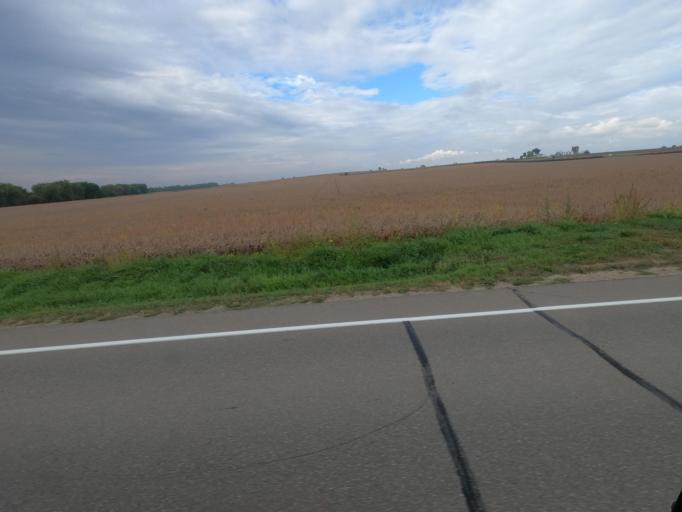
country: US
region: Iowa
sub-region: Henry County
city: Mount Pleasant
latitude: 40.7845
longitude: -91.5689
